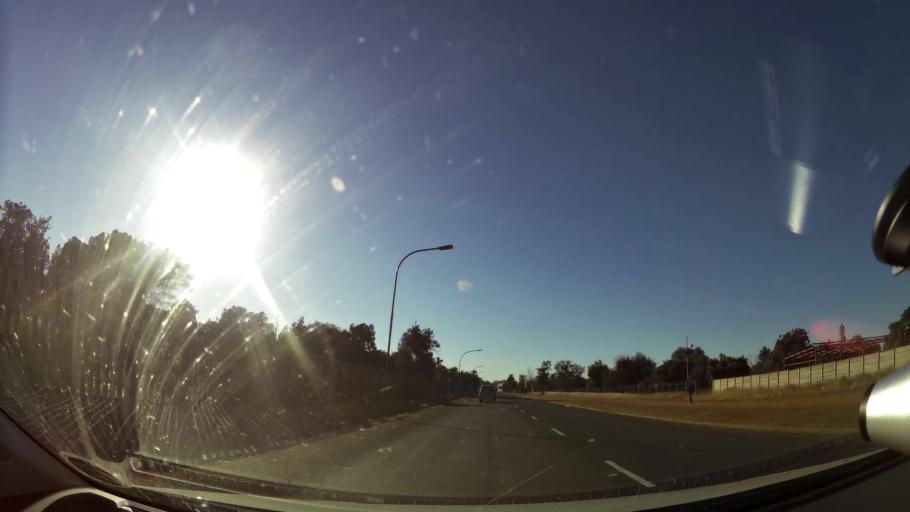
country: ZA
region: Northern Cape
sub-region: Frances Baard District Municipality
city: Kimberley
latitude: -28.7361
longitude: 24.7393
